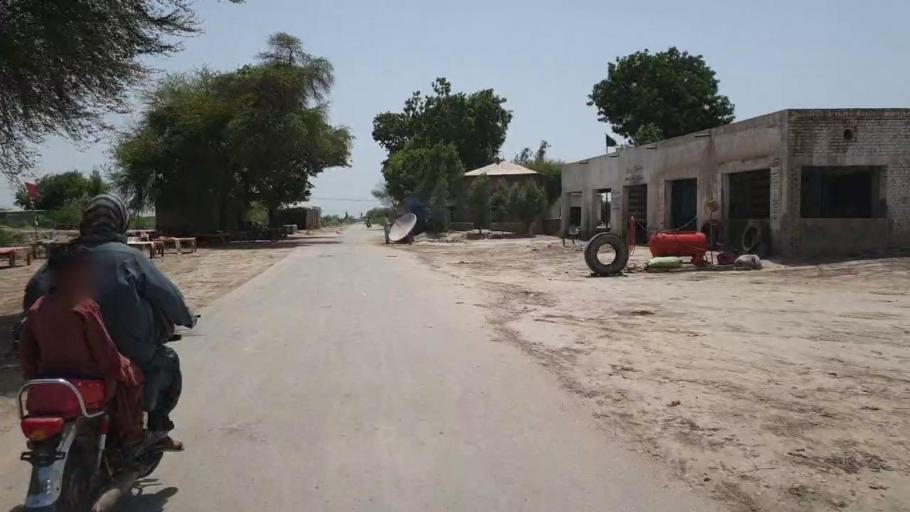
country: PK
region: Sindh
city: Daur
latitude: 26.3467
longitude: 68.1331
